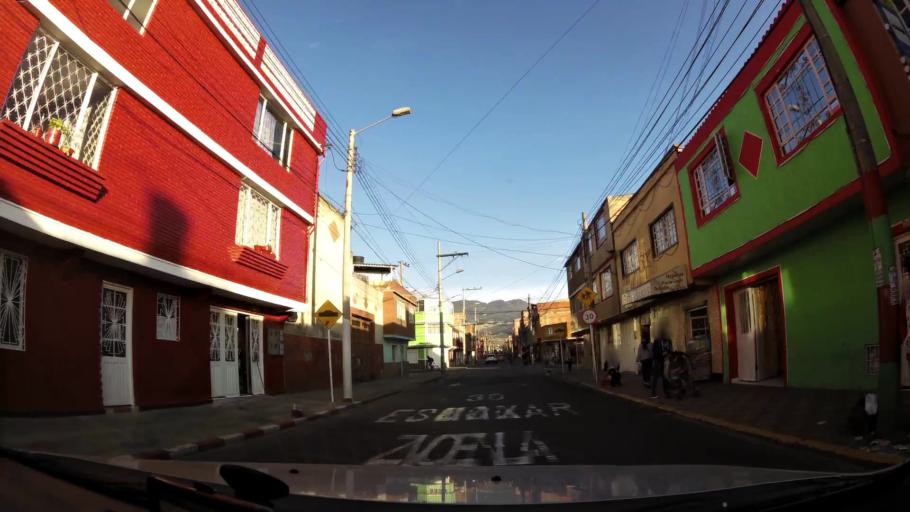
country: CO
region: Bogota D.C.
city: Bogota
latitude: 4.5674
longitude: -74.1329
